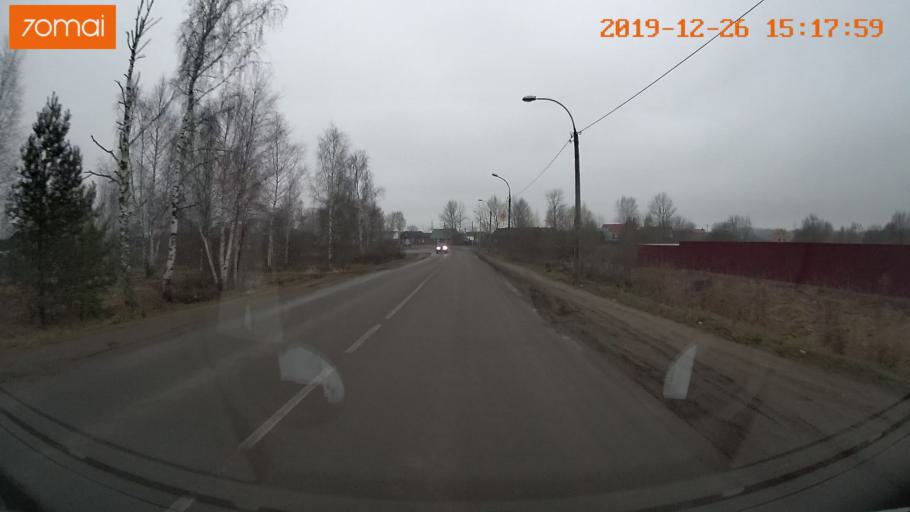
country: RU
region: Jaroslavl
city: Rybinsk
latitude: 58.0727
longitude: 38.8454
